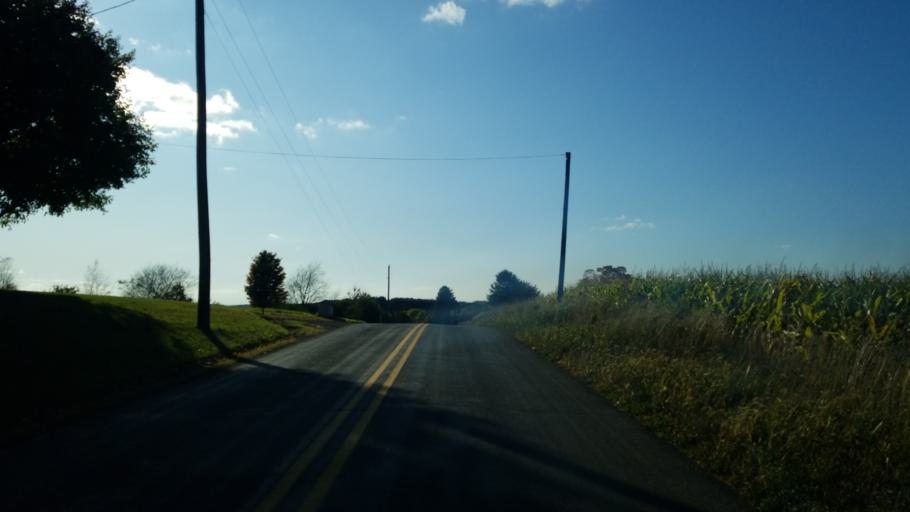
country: US
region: Pennsylvania
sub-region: Indiana County
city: Johnsonburg
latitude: 40.9033
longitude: -78.9094
